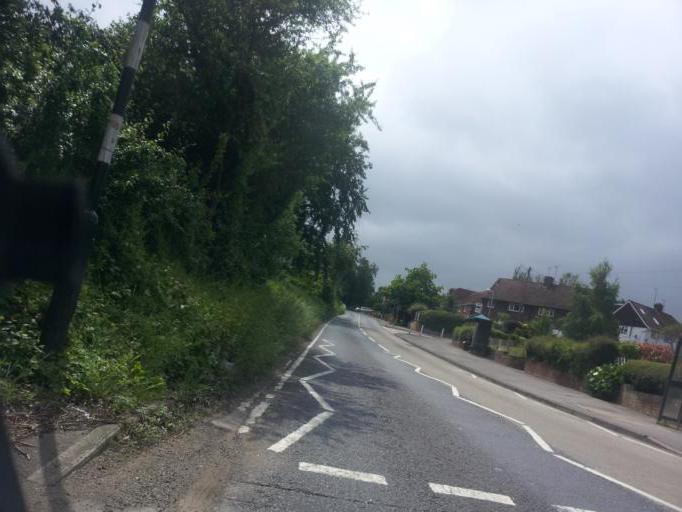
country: GB
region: England
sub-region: Kent
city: Wateringbury
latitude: 51.2473
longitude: 0.4157
